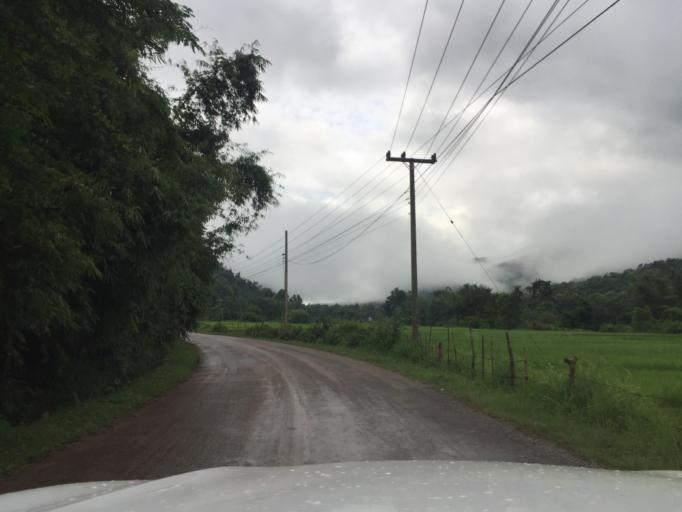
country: LA
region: Oudomxai
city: Muang La
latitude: 20.8457
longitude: 102.1053
